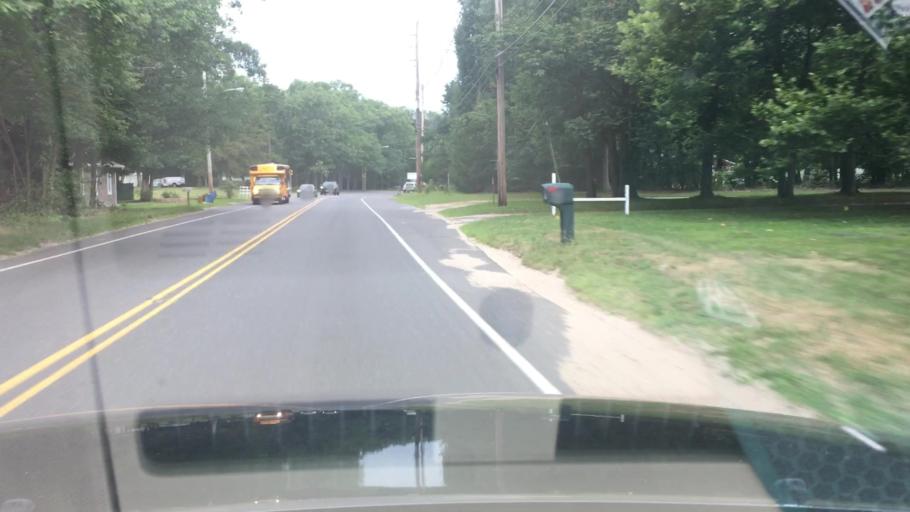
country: US
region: New Jersey
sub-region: Ocean County
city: Cedar Glen West
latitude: 40.0418
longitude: -74.3128
